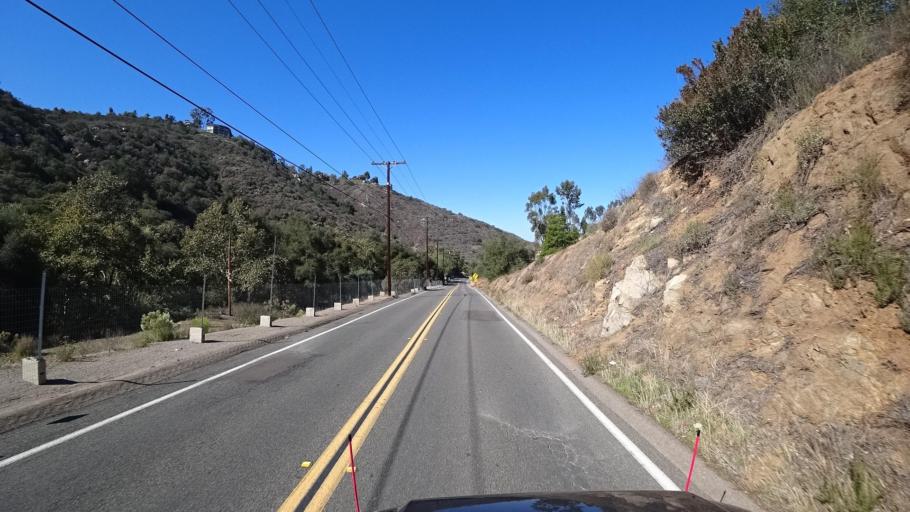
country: US
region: California
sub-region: San Diego County
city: Jamul
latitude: 32.7302
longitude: -116.8759
